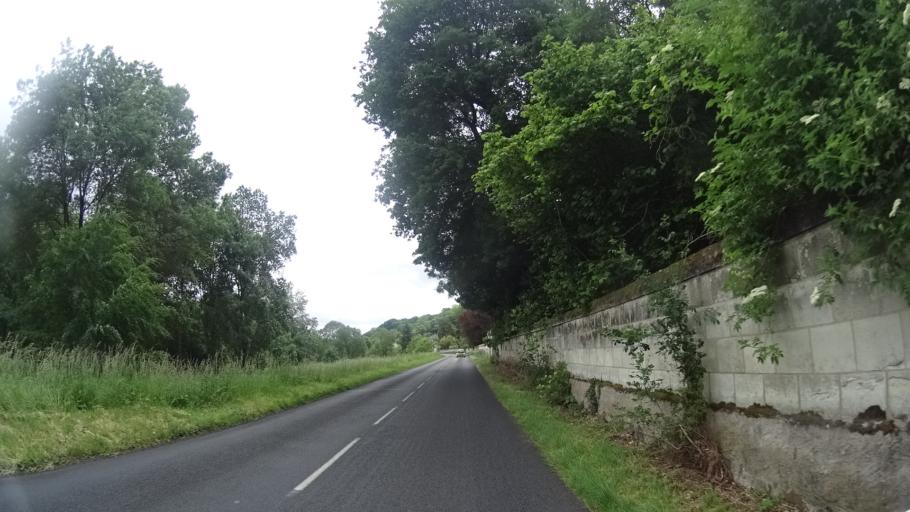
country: FR
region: Pays de la Loire
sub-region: Departement de Maine-et-Loire
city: Les Rosiers-sur-Loire
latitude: 47.3364
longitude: -0.2140
